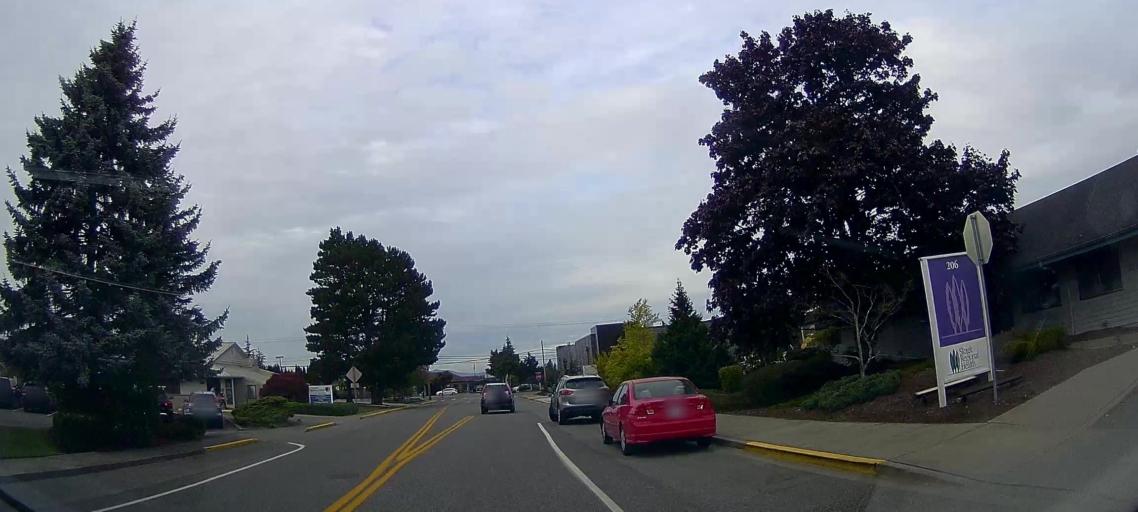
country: US
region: Washington
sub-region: Skagit County
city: Mount Vernon
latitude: 48.4201
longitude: -122.3251
